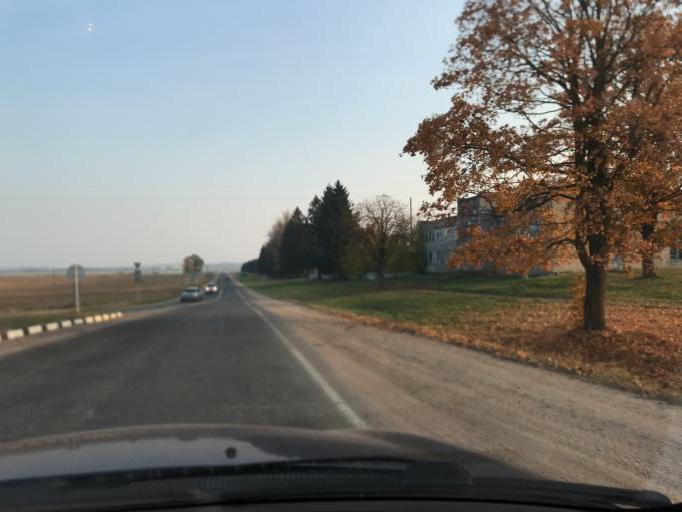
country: BY
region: Grodnenskaya
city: Karelichy
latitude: 53.5577
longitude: 26.1534
